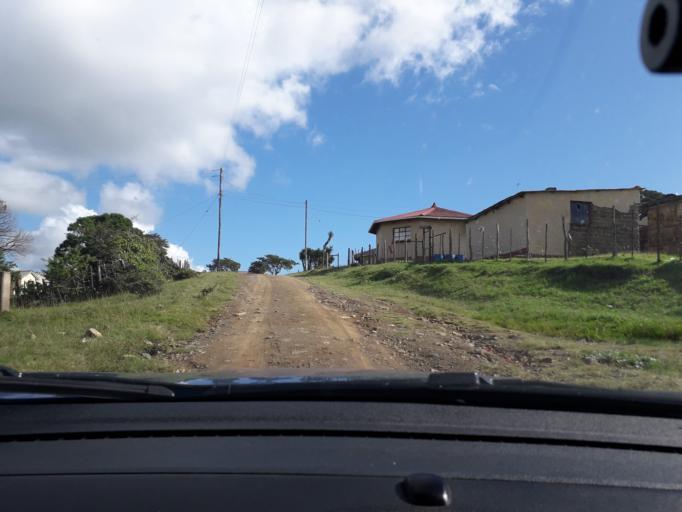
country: ZA
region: Eastern Cape
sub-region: Buffalo City Metropolitan Municipality
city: Bhisho
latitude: -33.1134
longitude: 27.4303
